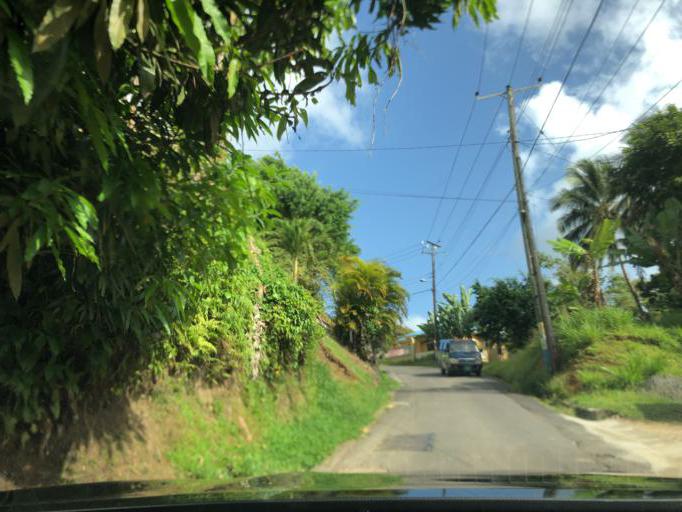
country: LC
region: Castries Quarter
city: Bisee
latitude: 13.9924
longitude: -60.9665
